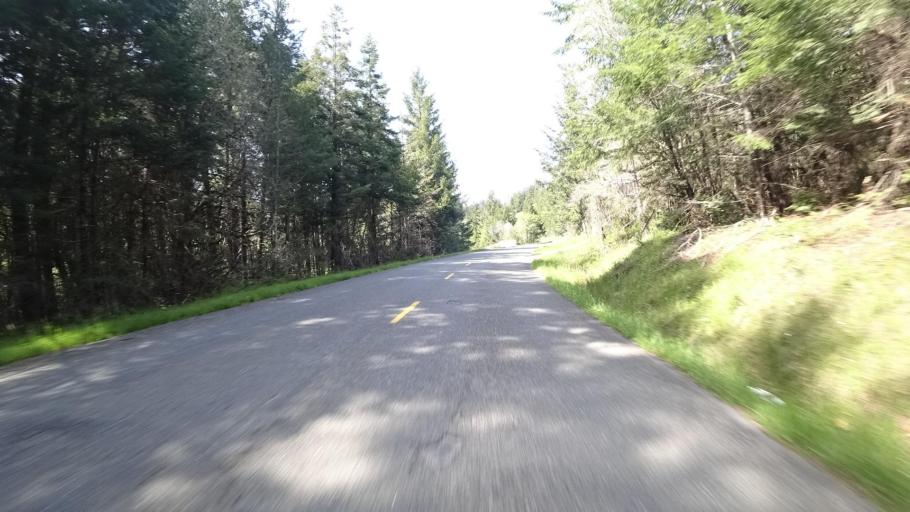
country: US
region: California
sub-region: Humboldt County
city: Rio Dell
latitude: 40.4457
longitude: -123.7955
